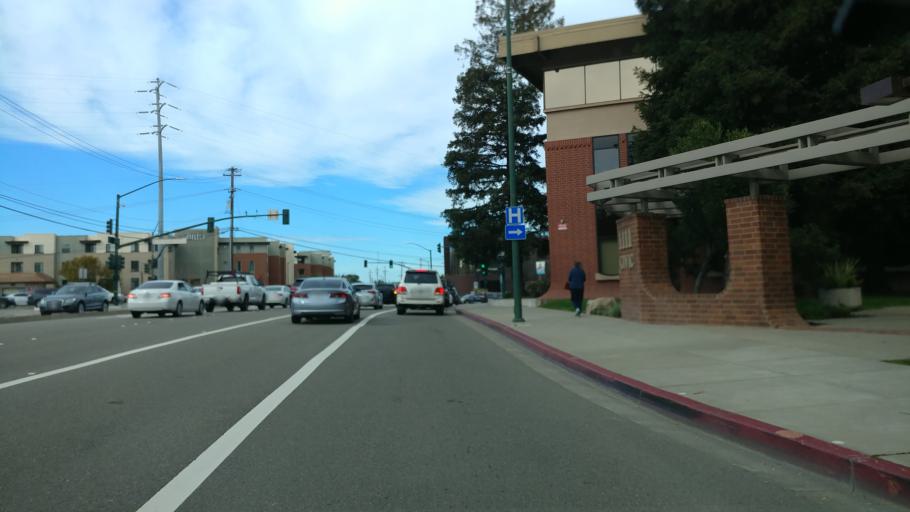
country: US
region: California
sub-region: Contra Costa County
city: Walnut Creek
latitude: 37.9058
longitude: -122.0589
